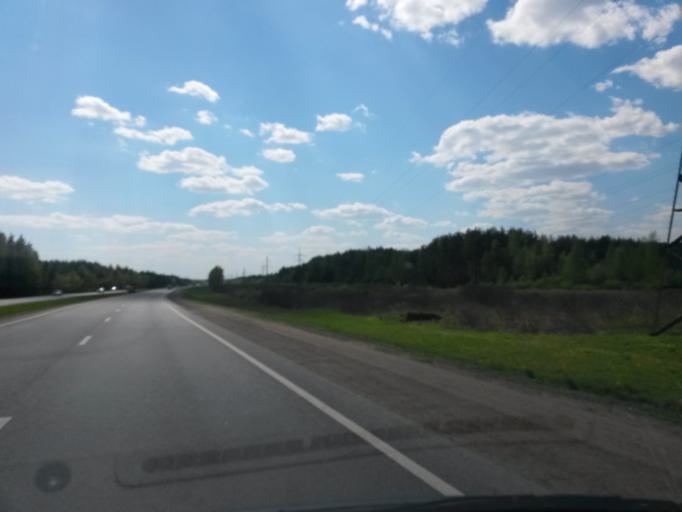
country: RU
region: Jaroslavl
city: Krasnyye Tkachi
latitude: 57.4902
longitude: 39.7813
